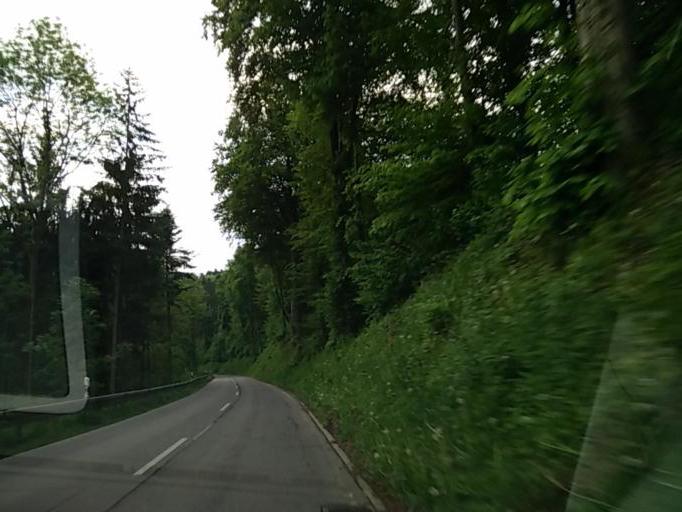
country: DE
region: Baden-Wuerttemberg
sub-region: Tuebingen Region
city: Hirrlingen
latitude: 48.4265
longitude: 8.8573
